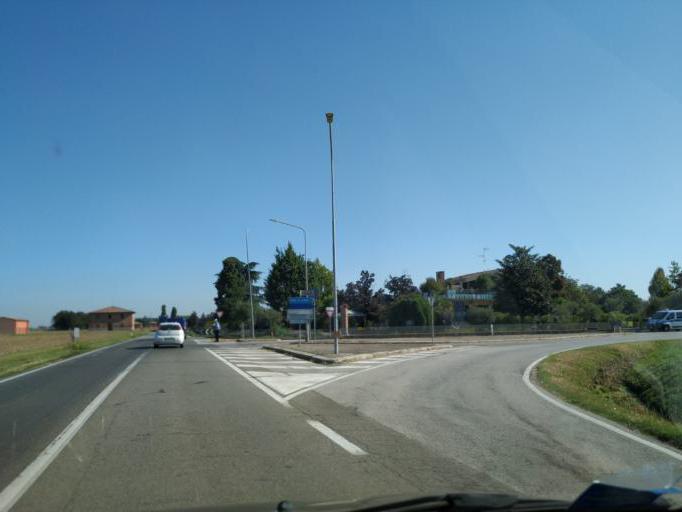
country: IT
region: Emilia-Romagna
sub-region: Provincia di Ferrara
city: Cento
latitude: 44.7245
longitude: 11.2579
